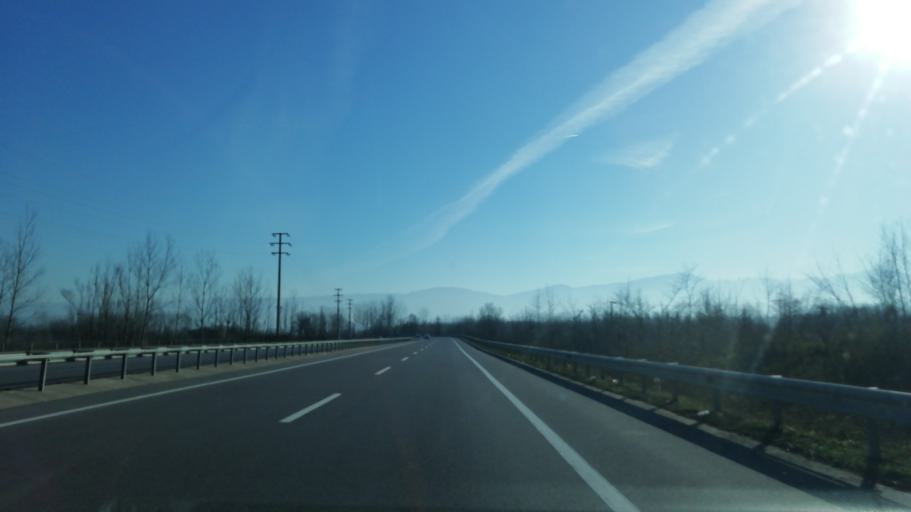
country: TR
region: Sakarya
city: Akyazi
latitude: 40.7014
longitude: 30.5674
